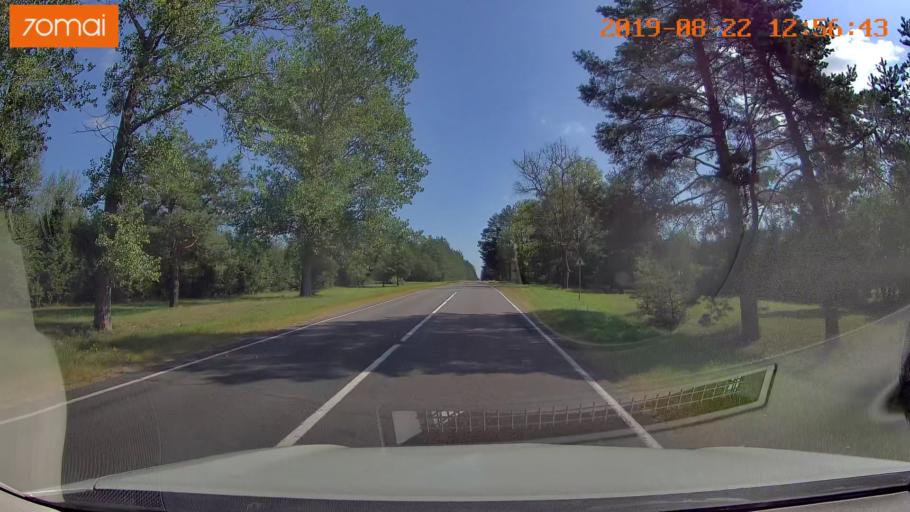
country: BY
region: Minsk
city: Prawdzinski
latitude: 53.4320
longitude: 27.7354
